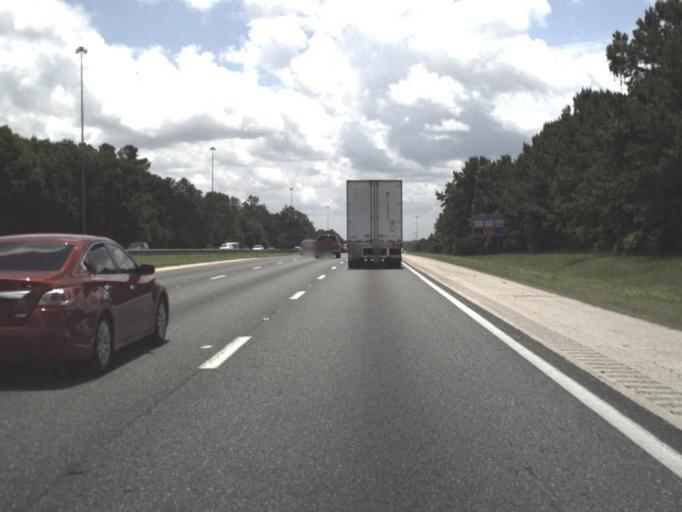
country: US
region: Florida
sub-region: Alachua County
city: Alachua
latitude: 29.6665
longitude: -82.4251
